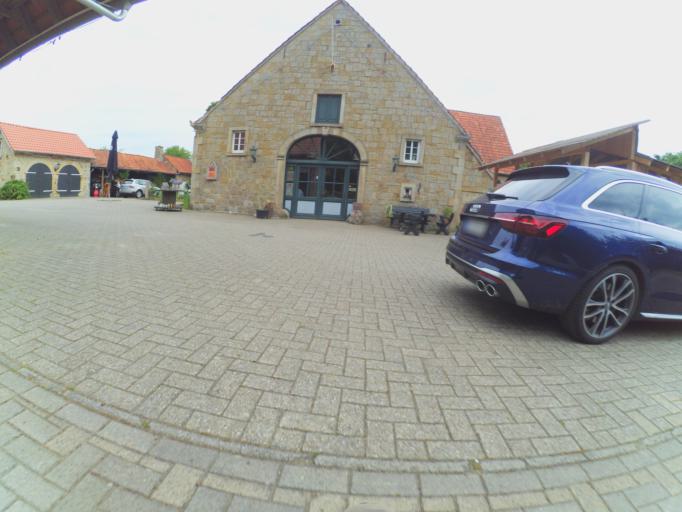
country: DE
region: North Rhine-Westphalia
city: Ibbenburen
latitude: 52.3134
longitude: 7.6740
